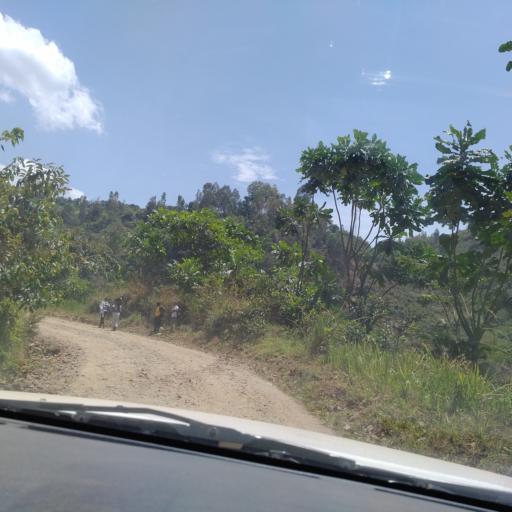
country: CD
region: Nord Kivu
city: Sake
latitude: -1.9674
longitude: 28.9150
